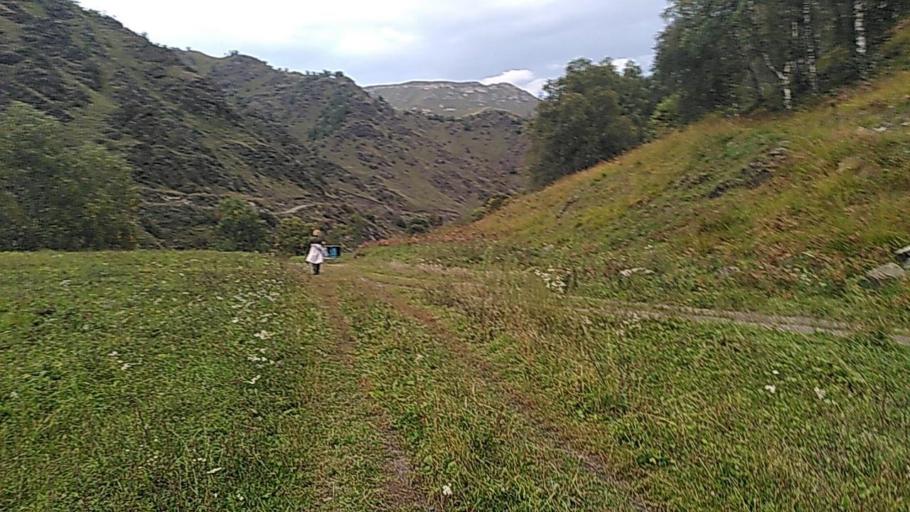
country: RU
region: Kabardino-Balkariya
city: Kamennomostskoye
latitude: 43.7183
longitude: 42.8422
